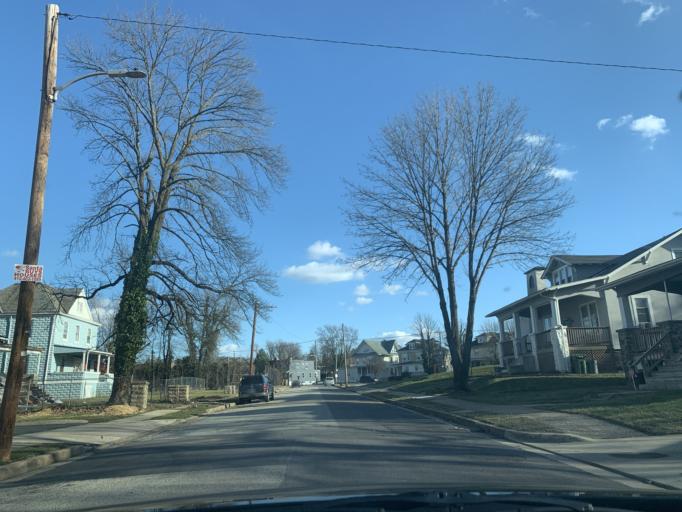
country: US
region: Maryland
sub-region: Baltimore County
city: Lochearn
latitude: 39.3258
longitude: -76.6859
